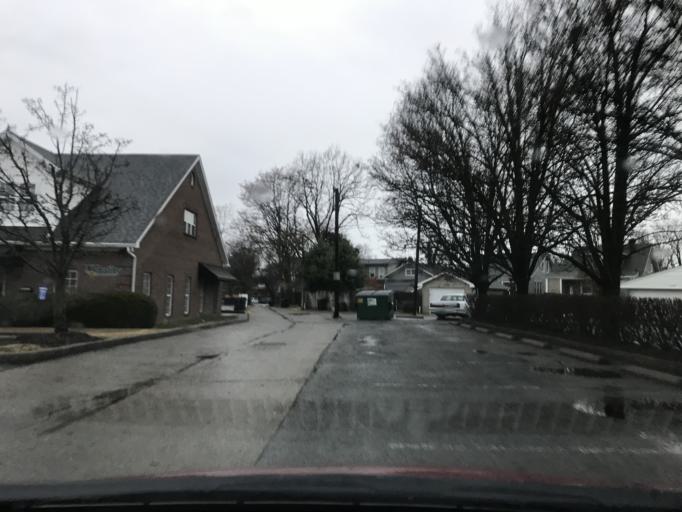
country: US
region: Kentucky
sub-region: Jefferson County
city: West Buechel
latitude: 38.2241
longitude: -85.6865
